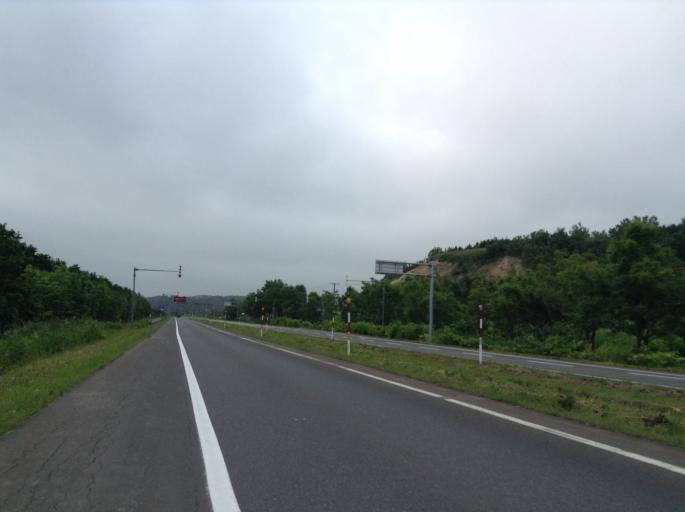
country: JP
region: Hokkaido
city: Wakkanai
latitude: 45.3671
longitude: 141.7280
